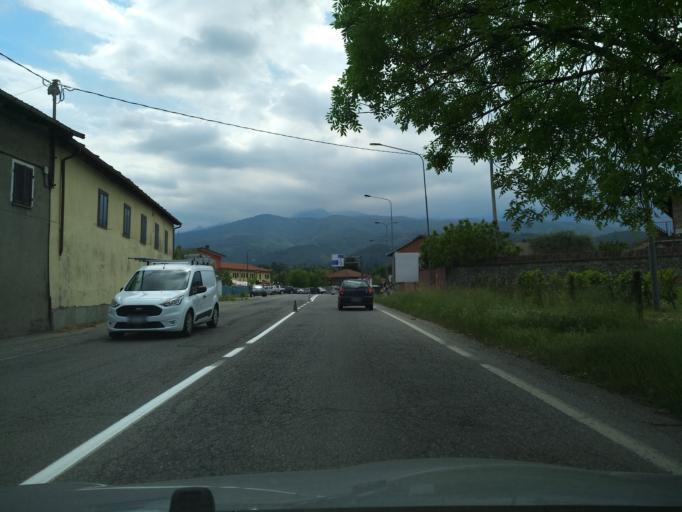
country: IT
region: Piedmont
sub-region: Provincia di Torino
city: Bibiana
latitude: 44.8101
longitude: 7.2910
